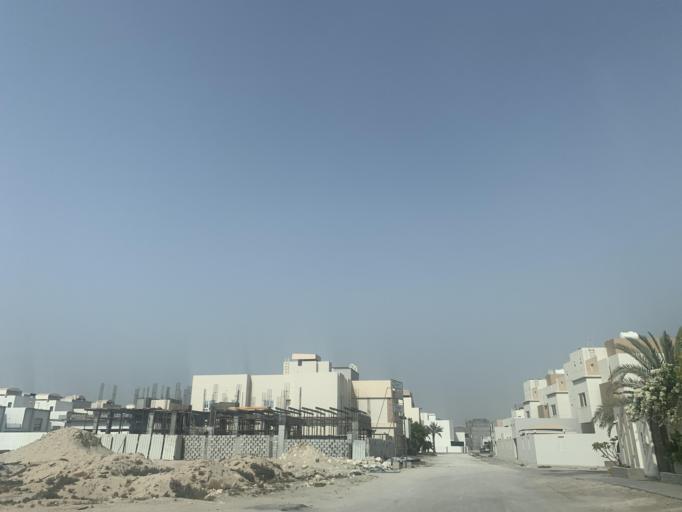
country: BH
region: Manama
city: Jidd Hafs
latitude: 26.2102
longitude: 50.4679
